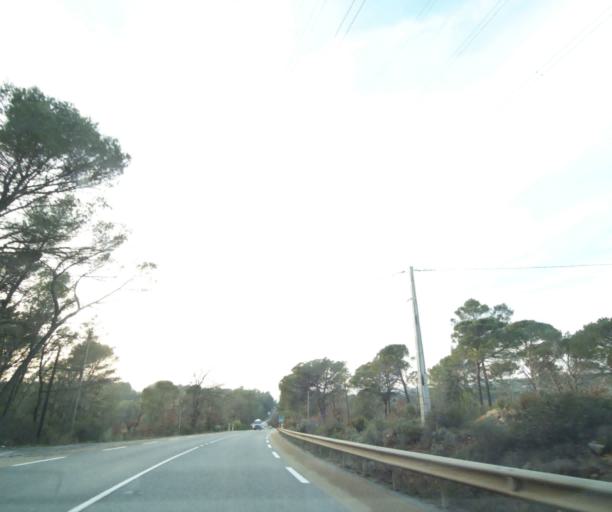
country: FR
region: Provence-Alpes-Cote d'Azur
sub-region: Departement du Var
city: La Motte
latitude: 43.5240
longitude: 6.5301
